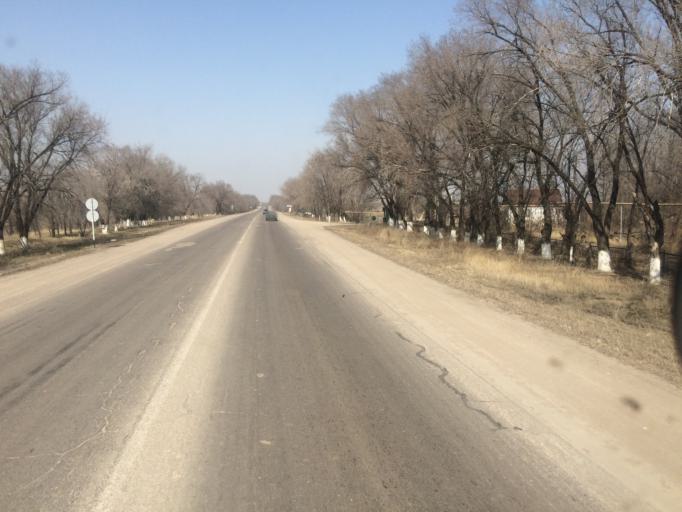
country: KZ
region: Almaty Oblysy
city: Burunday
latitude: 43.3089
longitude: 76.6664
